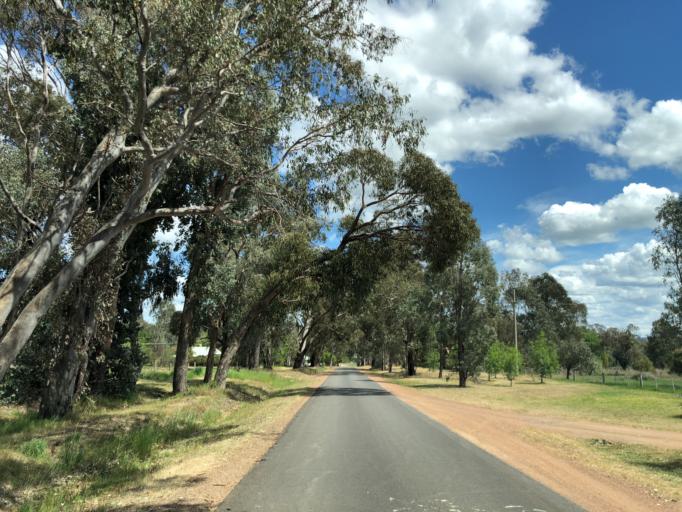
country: AU
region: Victoria
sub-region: Benalla
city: Benalla
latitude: -36.7290
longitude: 146.1126
